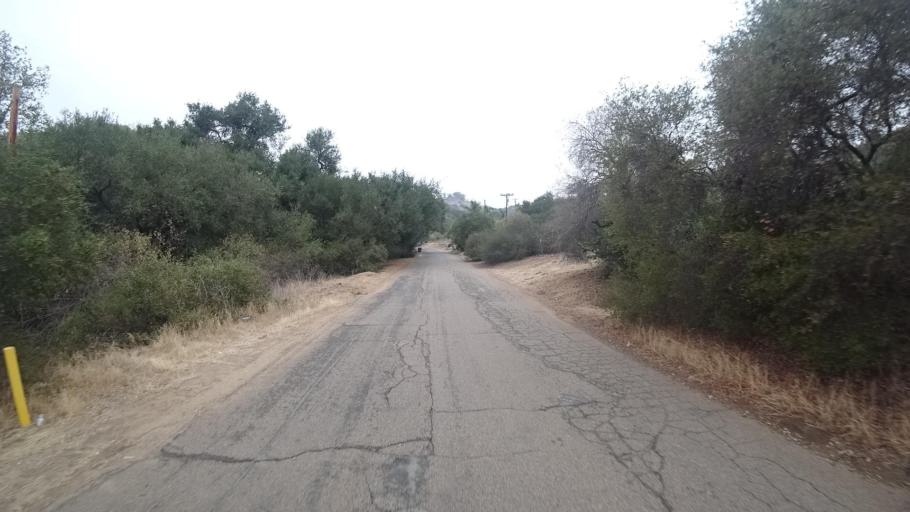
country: US
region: California
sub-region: San Diego County
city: Rainbow
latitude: 33.3728
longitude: -117.1613
